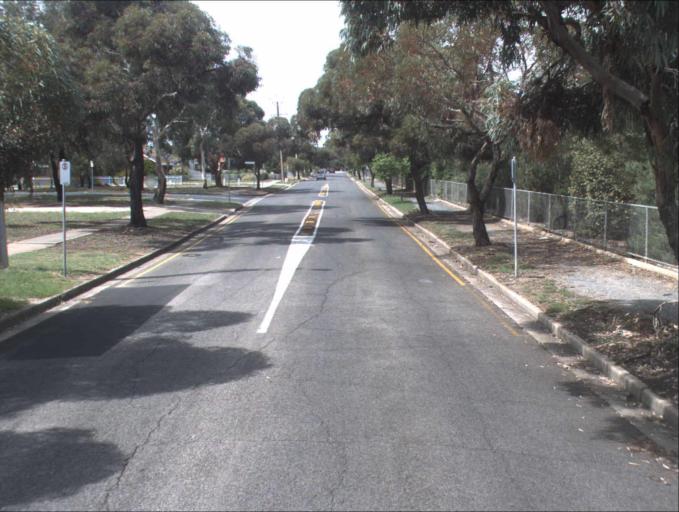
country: AU
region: South Australia
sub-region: Port Adelaide Enfield
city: Enfield
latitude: -34.8559
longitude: 138.6105
